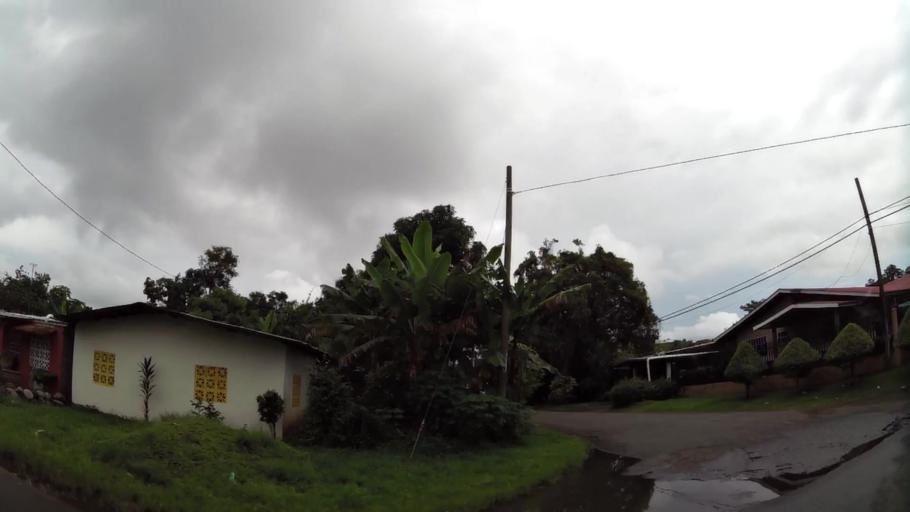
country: PA
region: Chiriqui
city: David
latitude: 8.4184
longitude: -82.4443
